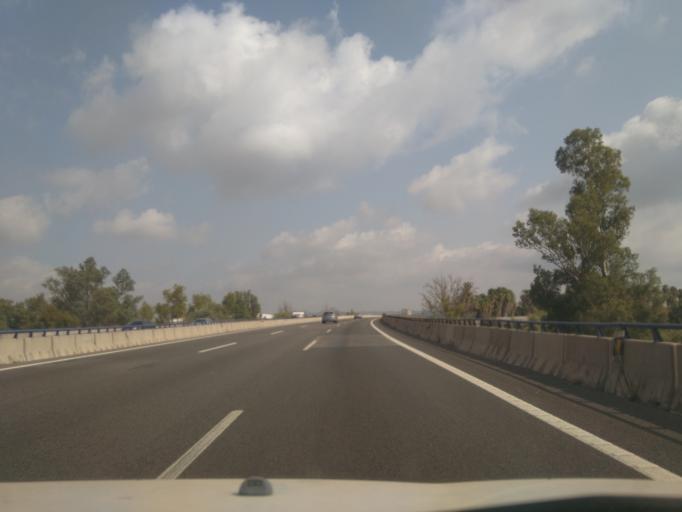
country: ES
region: Valencia
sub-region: Provincia de Valencia
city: L'Alcudia
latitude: 39.2067
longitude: -0.4982
